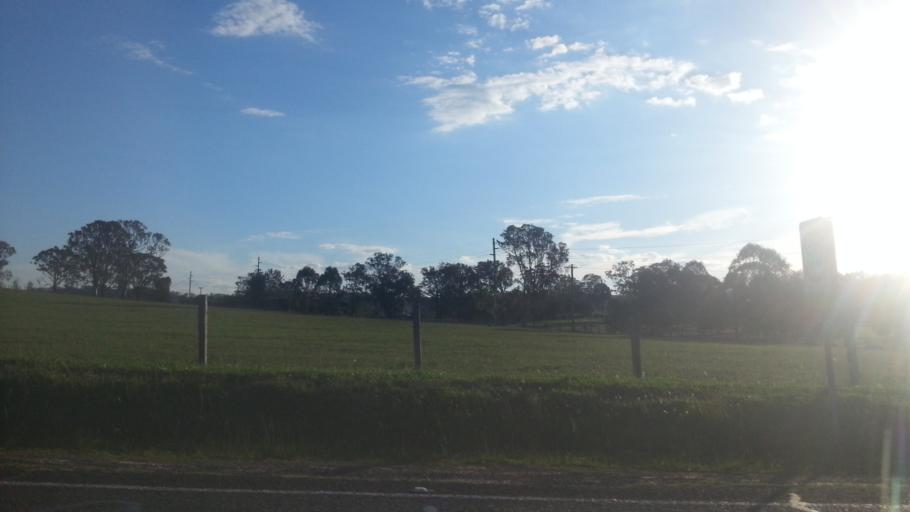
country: AU
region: New South Wales
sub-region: Wollondilly
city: Douglas Park
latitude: -34.1405
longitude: 150.7146
